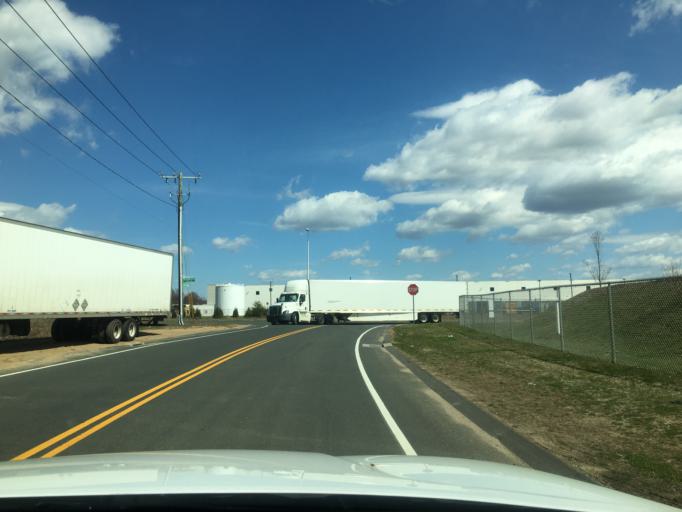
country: US
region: Connecticut
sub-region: Hartford County
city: Blue Hills
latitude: 41.8700
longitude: -72.7113
